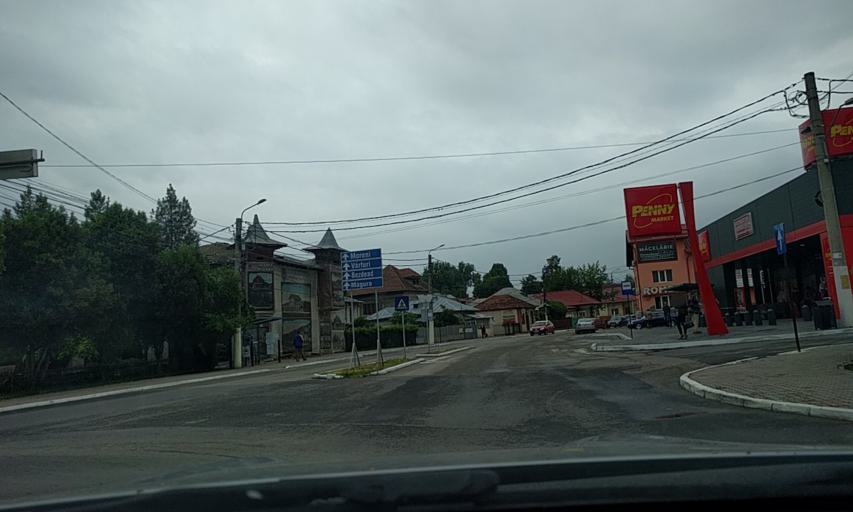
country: RO
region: Dambovita
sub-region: Oras Pucioasa
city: Pucioasa
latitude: 45.0779
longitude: 25.4336
